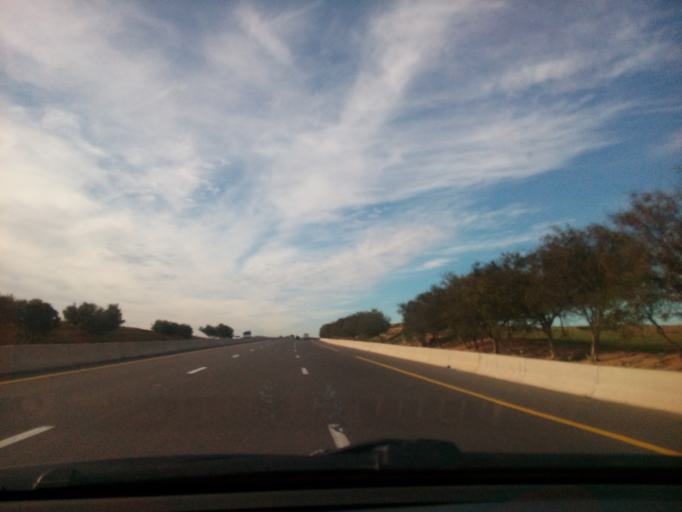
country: DZ
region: Sidi Bel Abbes
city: Sidi Bel Abbes
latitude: 35.1931
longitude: -0.7016
